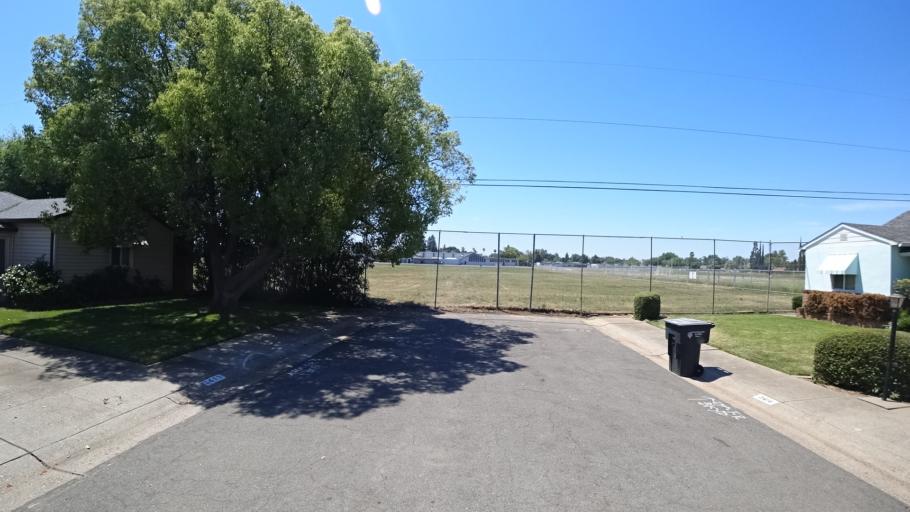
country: US
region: California
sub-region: Sacramento County
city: Florin
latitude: 38.5434
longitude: -121.4260
